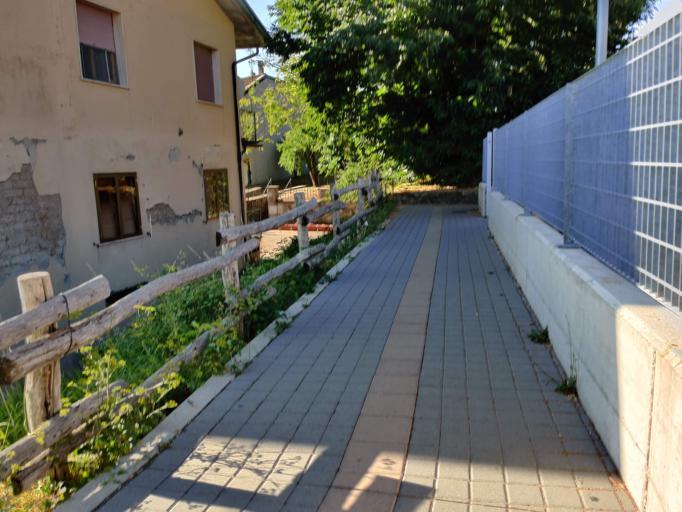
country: IT
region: Tuscany
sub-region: Provincia di Siena
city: Abbadia San Salvatore
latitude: 42.8827
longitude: 11.6745
